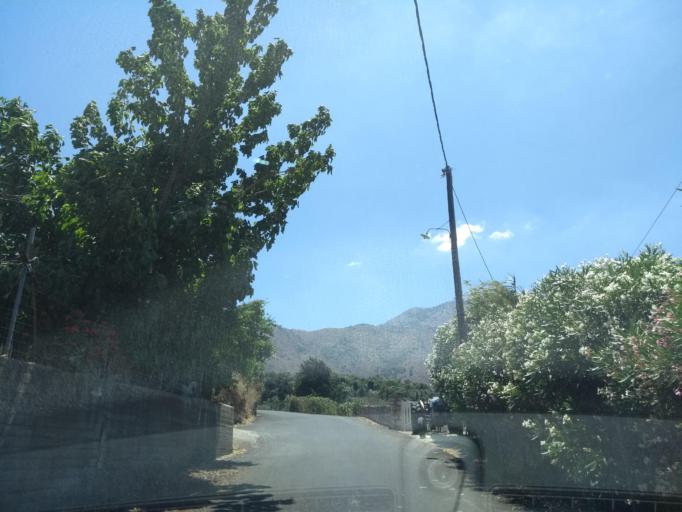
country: GR
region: Crete
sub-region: Nomos Chanias
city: Georgioupolis
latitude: 35.3160
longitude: 24.3087
